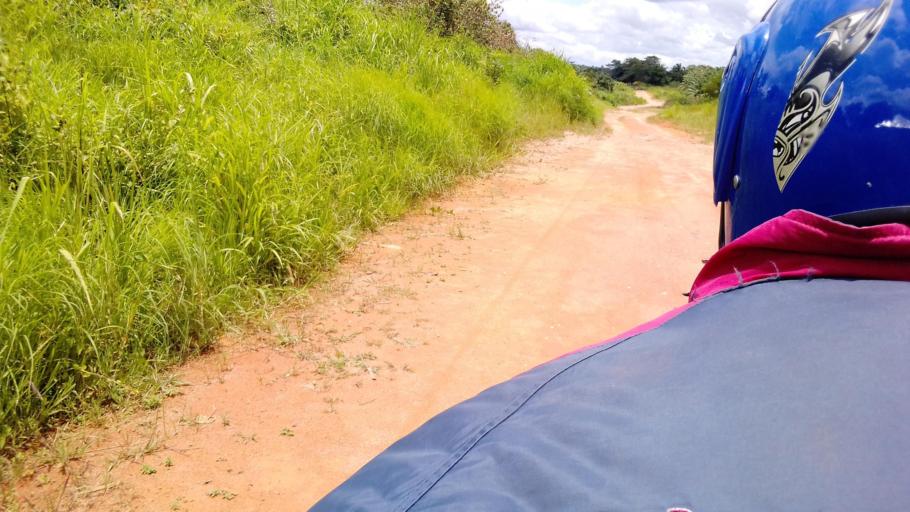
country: SL
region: Eastern Province
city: Koidu
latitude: 8.6776
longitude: -10.9551
